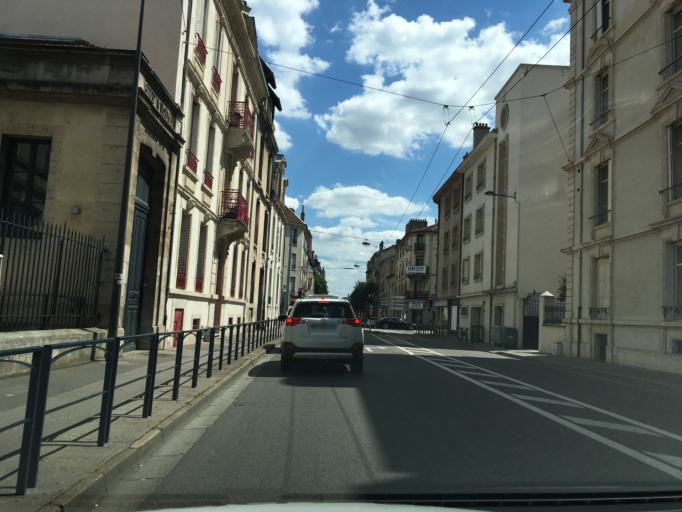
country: FR
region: Lorraine
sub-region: Departement de Meurthe-et-Moselle
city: Nancy
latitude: 48.6900
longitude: 6.1694
